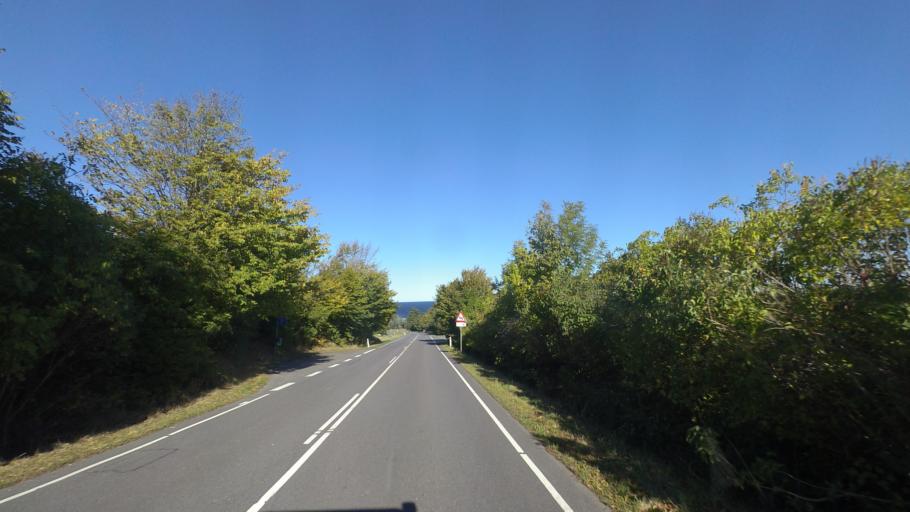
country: DK
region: Capital Region
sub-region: Bornholm Kommune
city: Akirkeby
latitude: 55.1729
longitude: 15.0251
